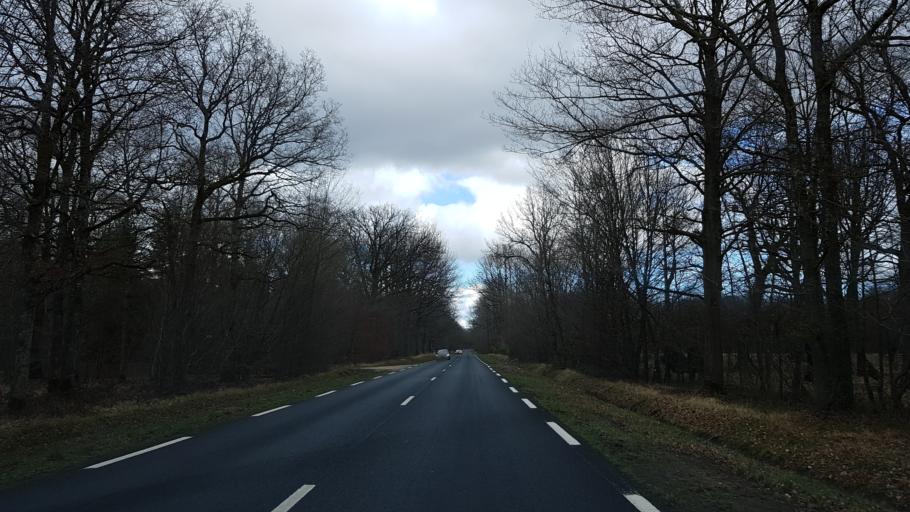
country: FR
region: Ile-de-France
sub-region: Departement des Yvelines
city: Rambouillet
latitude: 48.6309
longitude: 1.8850
